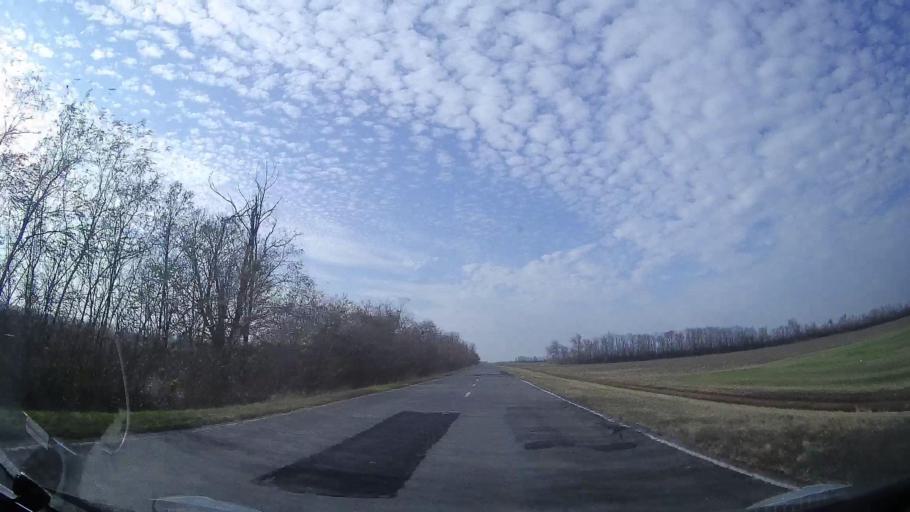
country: RU
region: Rostov
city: Veselyy
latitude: 46.9693
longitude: 40.7119
